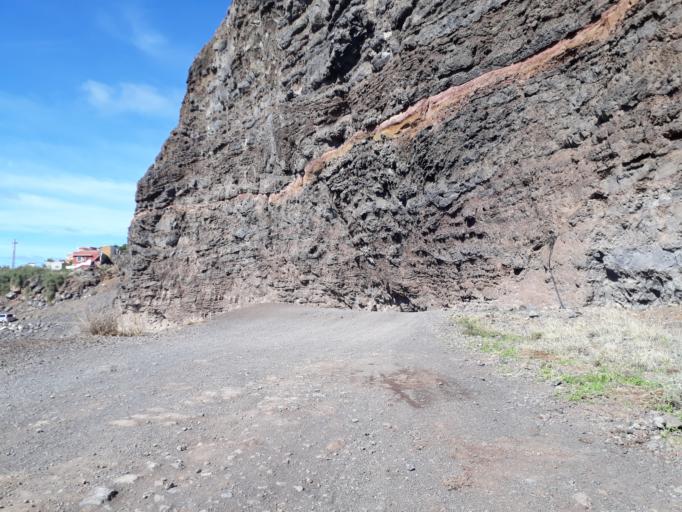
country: ES
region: Canary Islands
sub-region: Provincia de Santa Cruz de Tenerife
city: Alajero
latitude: 28.0819
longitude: -17.3305
